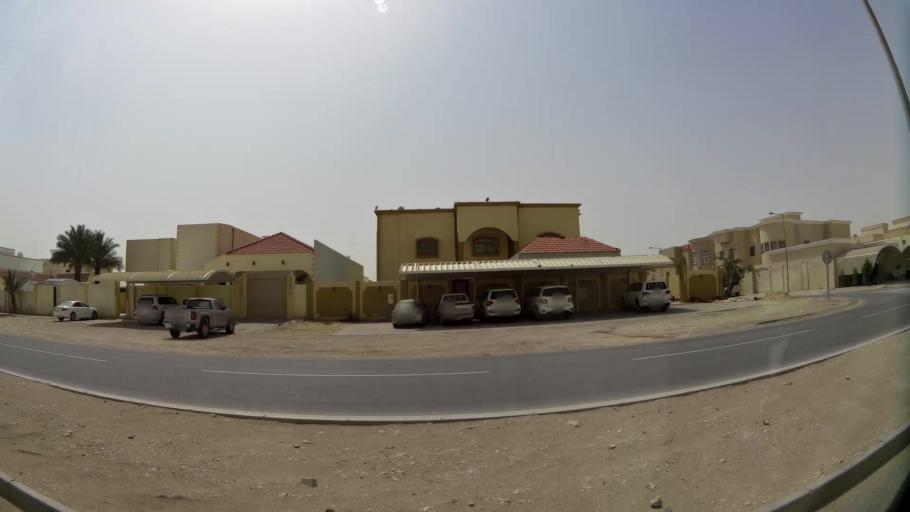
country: QA
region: Baladiyat ar Rayyan
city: Ar Rayyan
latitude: 25.2476
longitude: 51.3774
